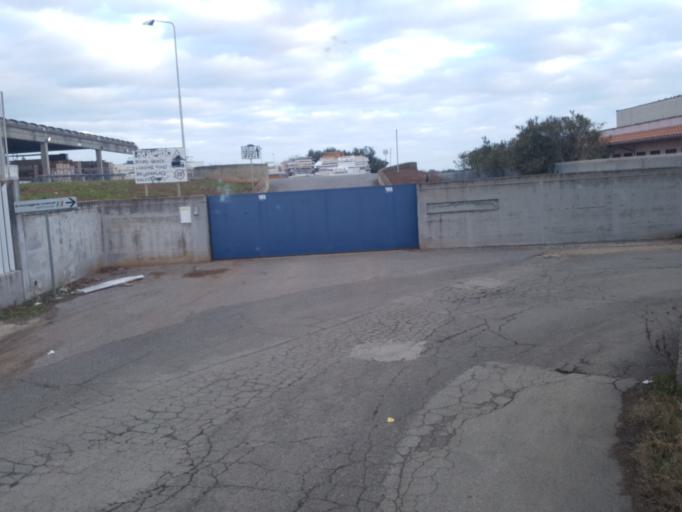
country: IT
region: Latium
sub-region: Citta metropolitana di Roma Capitale
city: Area Produttiva
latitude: 41.6997
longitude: 12.5420
